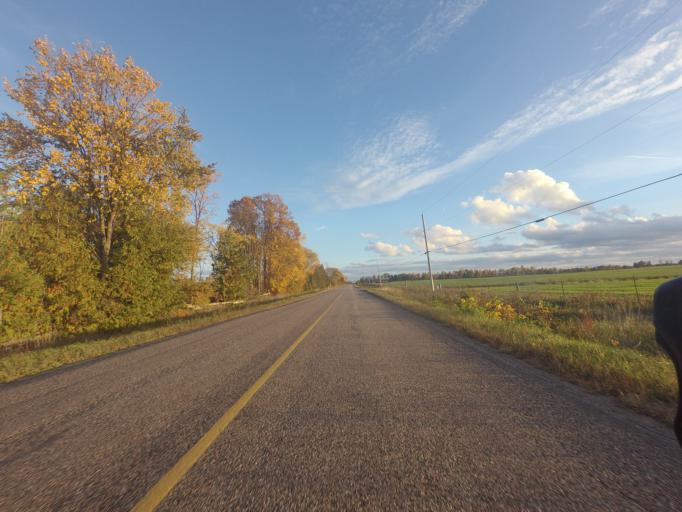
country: CA
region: Ontario
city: Renfrew
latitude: 45.4529
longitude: -76.9714
